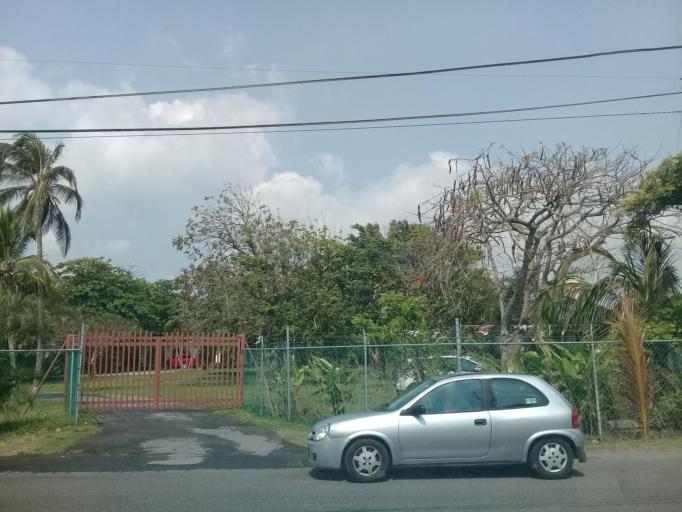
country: MX
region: Veracruz
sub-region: Veracruz
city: Hacienda Sotavento
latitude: 19.1318
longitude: -96.1775
